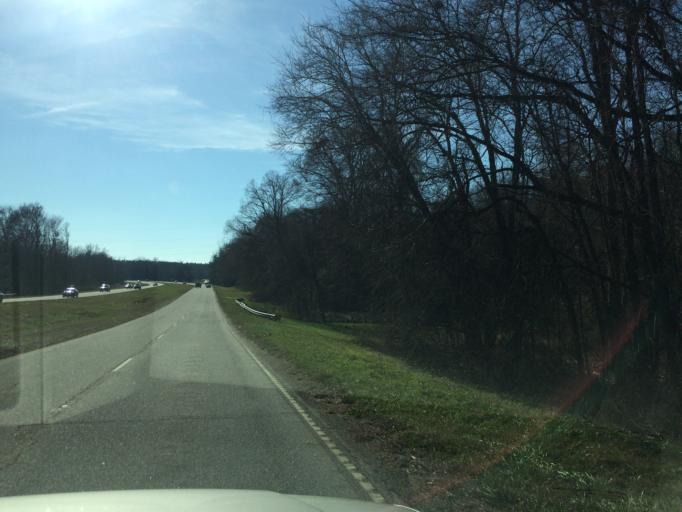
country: US
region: South Carolina
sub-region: Greenwood County
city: Greenwood
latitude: 34.2508
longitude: -82.0962
